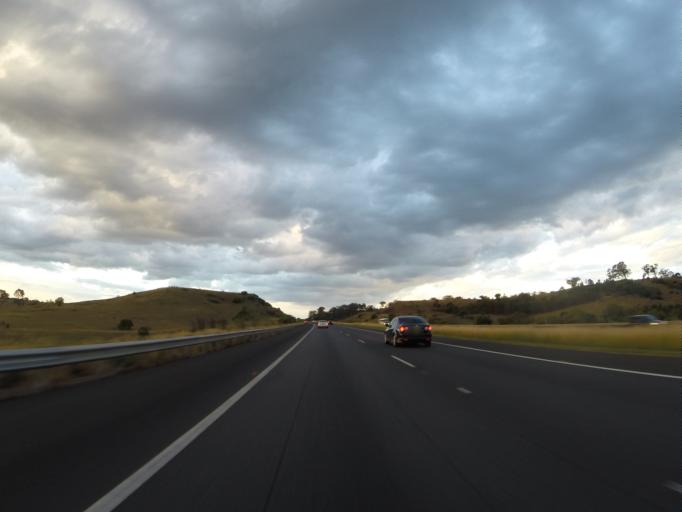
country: AU
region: New South Wales
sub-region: Campbelltown Municipality
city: Glen Alpine
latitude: -34.1166
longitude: 150.7582
